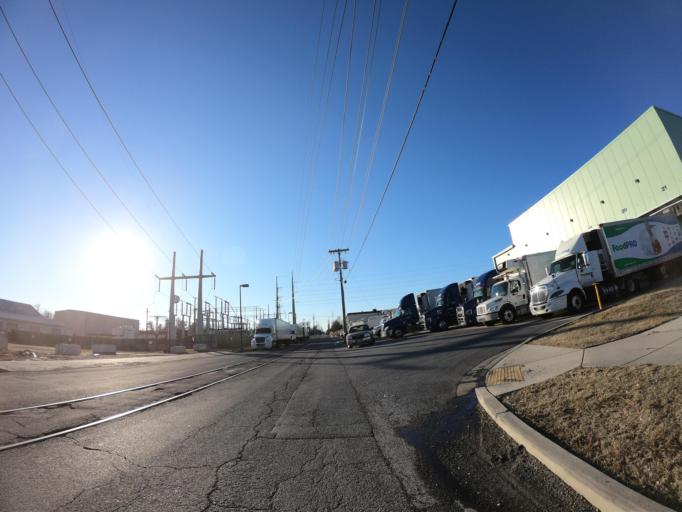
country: US
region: Maryland
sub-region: Frederick County
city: Frederick
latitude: 39.4198
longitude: -77.4011
